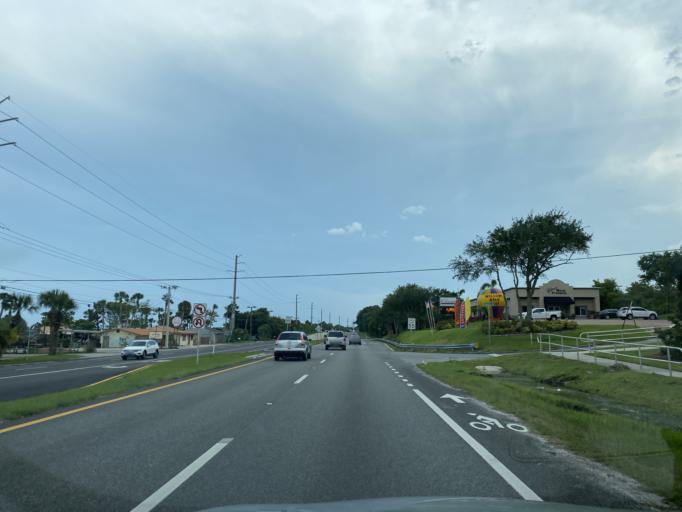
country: US
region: Florida
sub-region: Brevard County
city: South Patrick Shores
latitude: 28.2285
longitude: -80.6726
